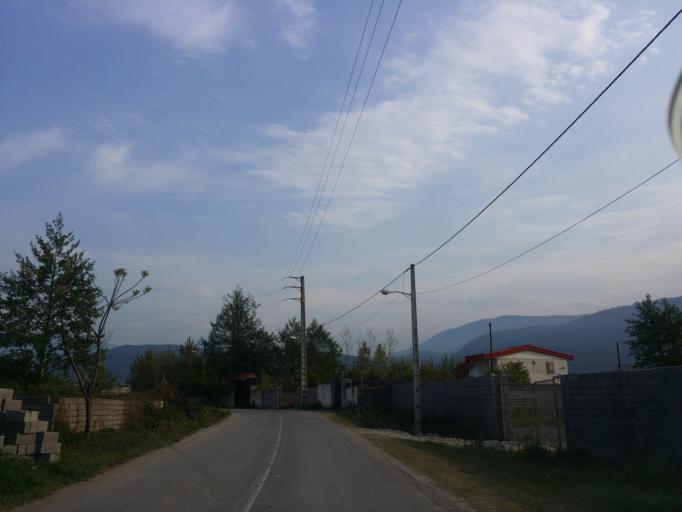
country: IR
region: Mazandaran
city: Chalus
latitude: 36.6797
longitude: 51.3721
